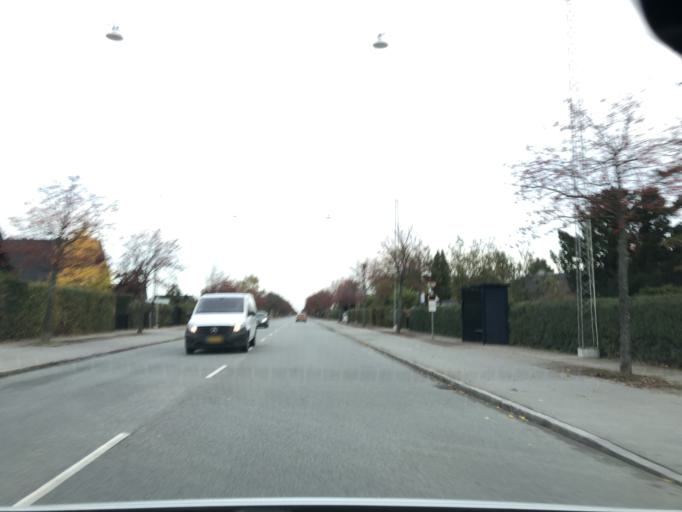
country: DK
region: Capital Region
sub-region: Tarnby Kommune
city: Tarnby
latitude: 55.5940
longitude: 12.5818
